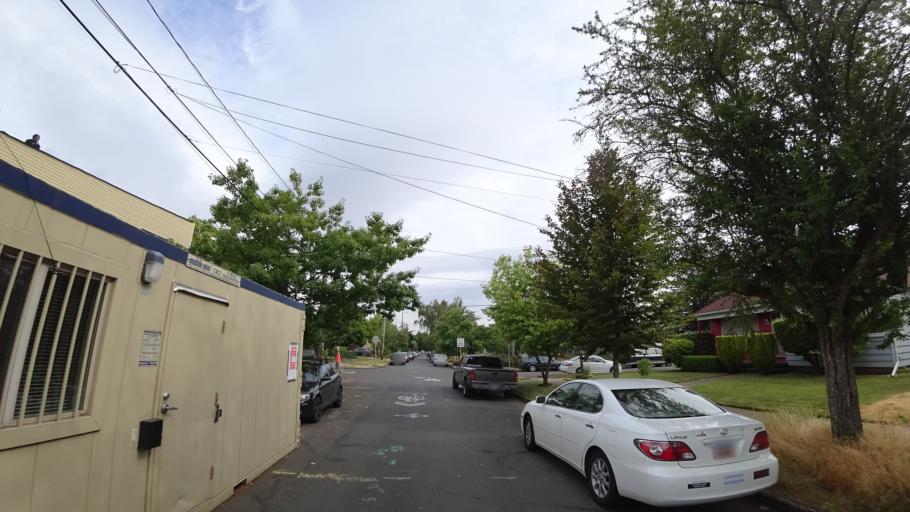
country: US
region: Oregon
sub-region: Multnomah County
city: Portland
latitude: 45.5732
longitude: -122.6832
